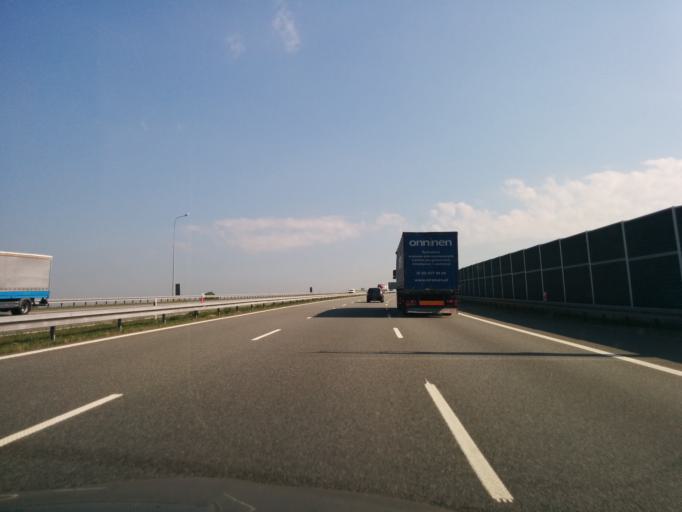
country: PL
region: Silesian Voivodeship
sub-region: Powiat tarnogorski
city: Wieszowa
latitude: 50.3525
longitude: 18.7240
